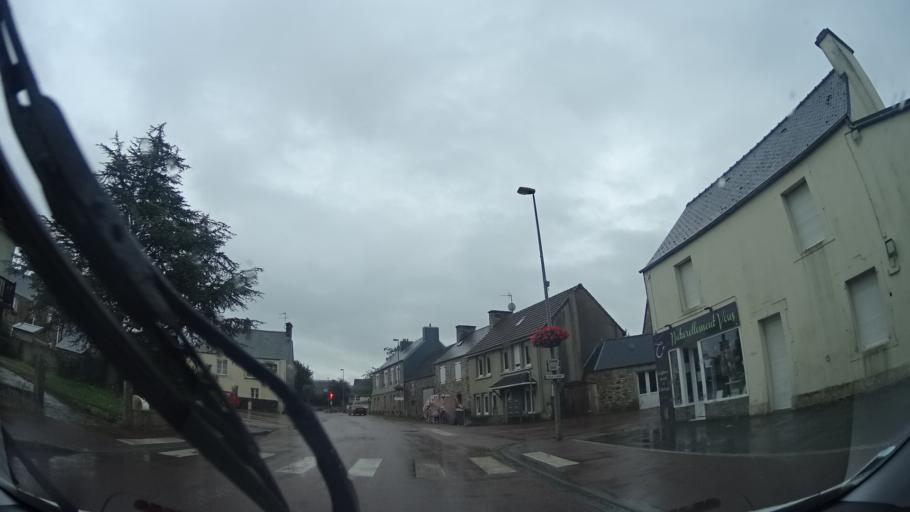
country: FR
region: Lower Normandy
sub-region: Departement de la Manche
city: Urville-Nacqueville
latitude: 49.5952
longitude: -1.7742
